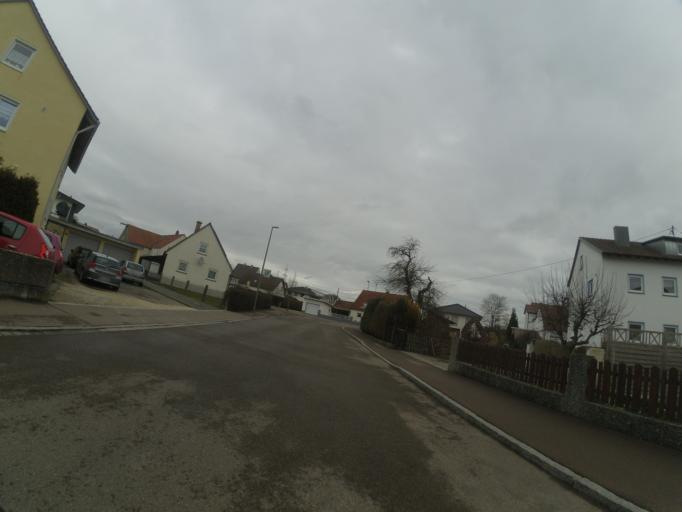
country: DE
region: Bavaria
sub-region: Swabia
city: Senden
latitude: 48.2983
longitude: 10.0536
